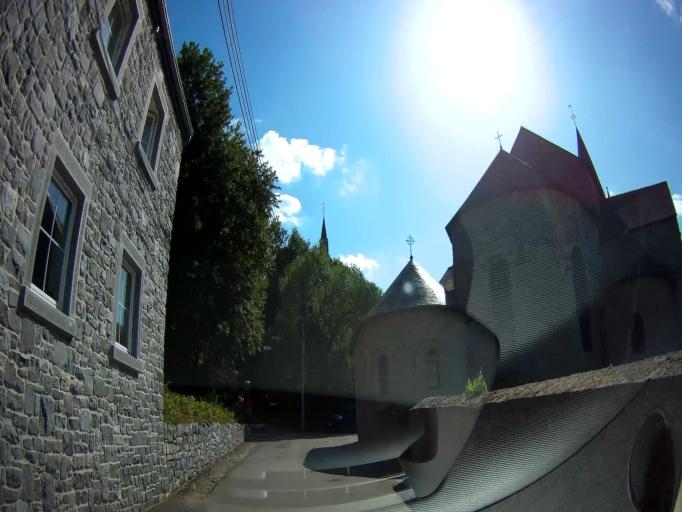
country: BE
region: Wallonia
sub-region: Province de Namur
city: Houyet
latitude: 50.2291
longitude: 5.0085
